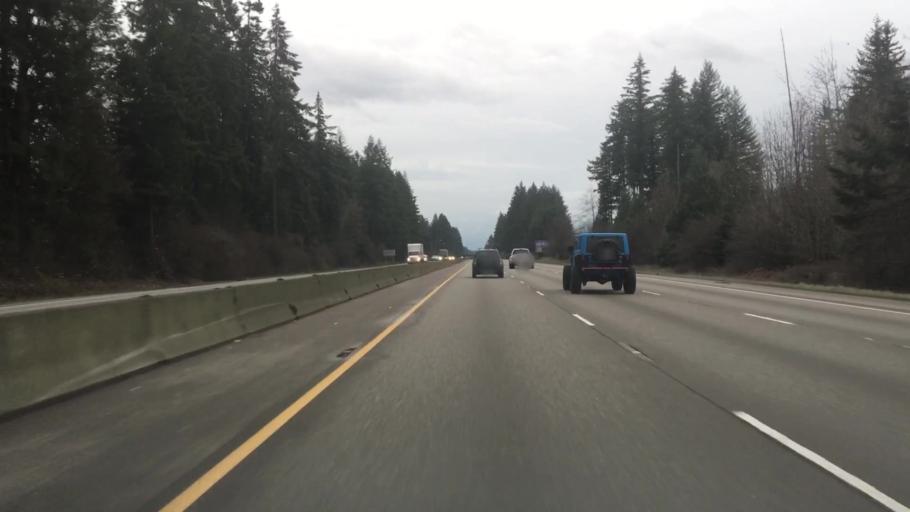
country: US
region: Washington
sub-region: Thurston County
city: Tumwater
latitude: 46.9627
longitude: -122.9346
